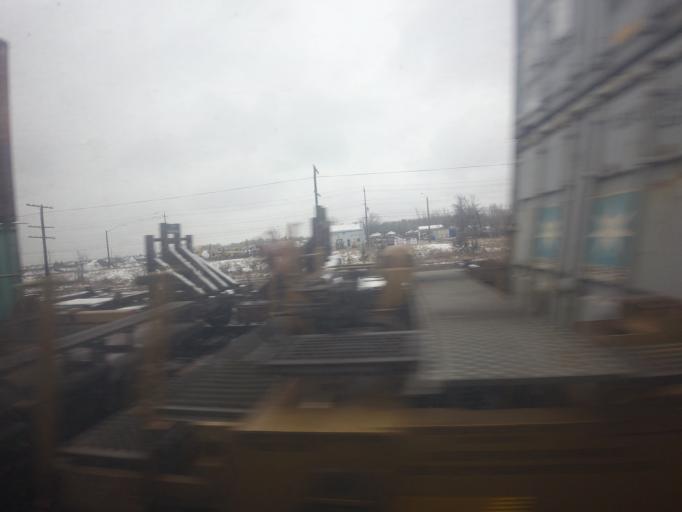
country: CA
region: Ontario
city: Belleville
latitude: 44.1837
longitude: -77.3593
